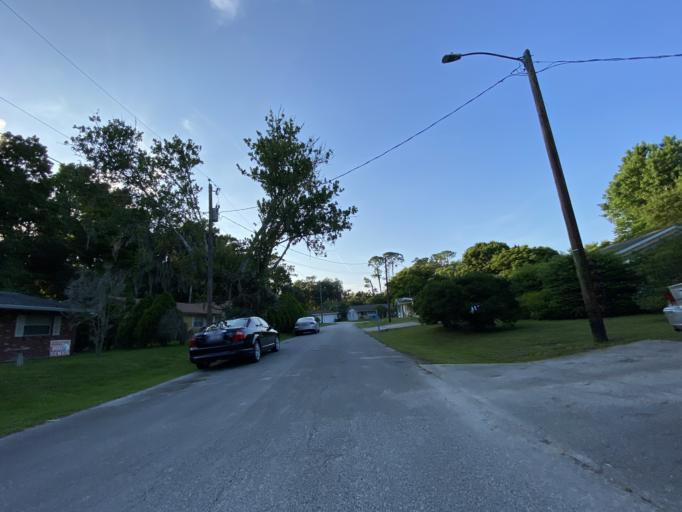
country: US
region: Florida
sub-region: Volusia County
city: Port Orange
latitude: 29.1457
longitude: -81.0042
